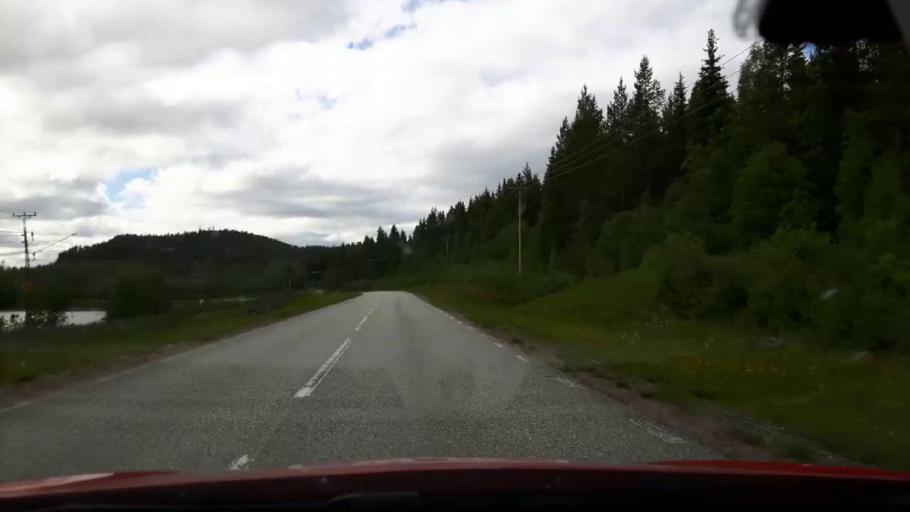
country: SE
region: Jaemtland
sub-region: Ragunda Kommun
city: Hammarstrand
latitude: 62.9658
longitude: 16.0167
